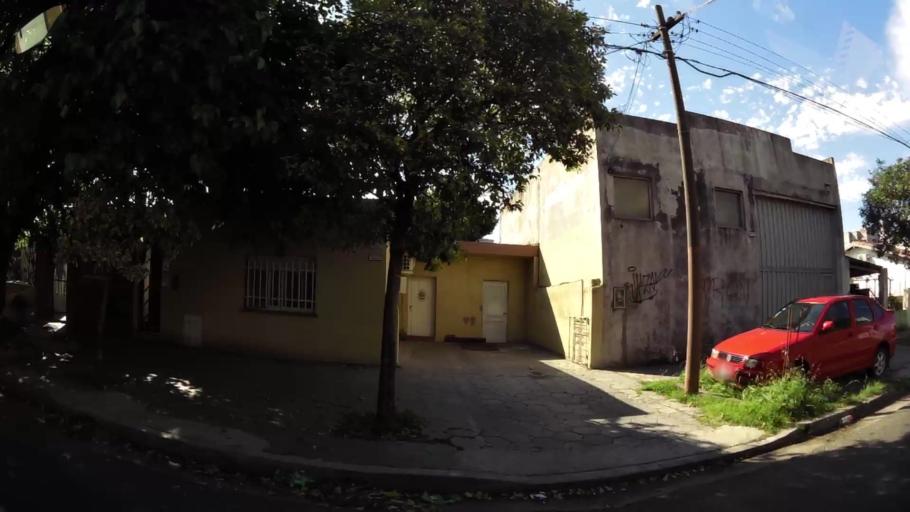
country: AR
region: Buenos Aires
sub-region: Partido de Moron
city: Moron
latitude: -34.6596
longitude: -58.5911
